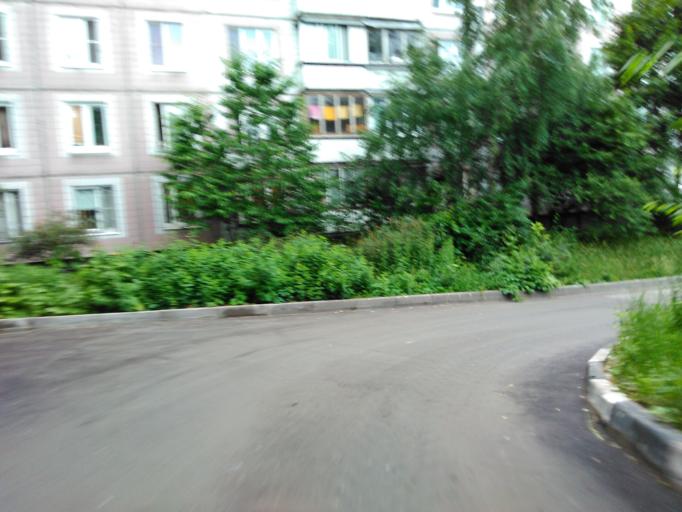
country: RU
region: Moscow
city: Yasenevo
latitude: 55.6116
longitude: 37.5502
